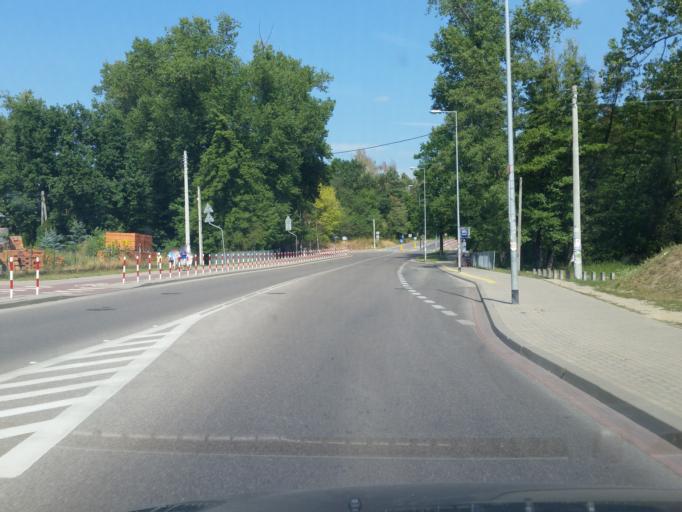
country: PL
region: Masovian Voivodeship
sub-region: Warszawa
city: Bialoleka
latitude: 52.3377
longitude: 20.9427
